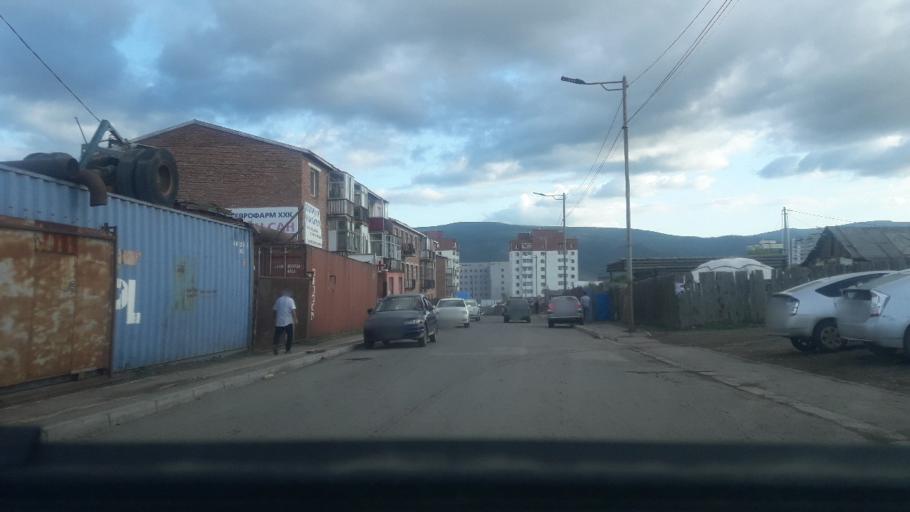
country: MN
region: Ulaanbaatar
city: Ulaanbaatar
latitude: 47.9197
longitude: 106.9954
